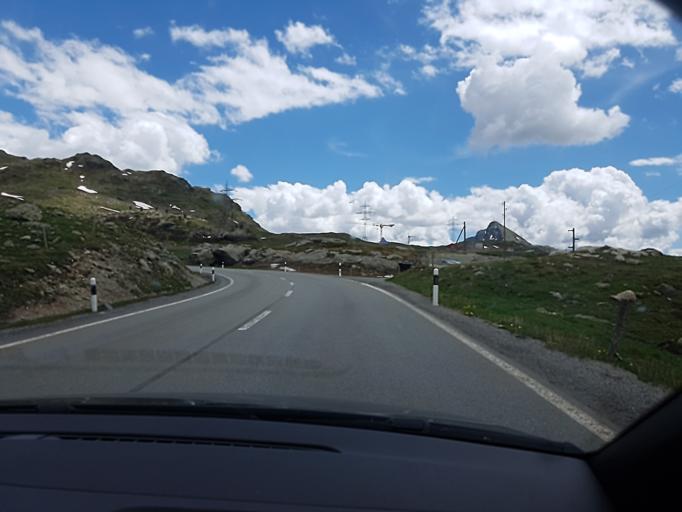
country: CH
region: Grisons
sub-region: Bernina District
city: Poschiavo
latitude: 46.4158
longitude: 10.0144
